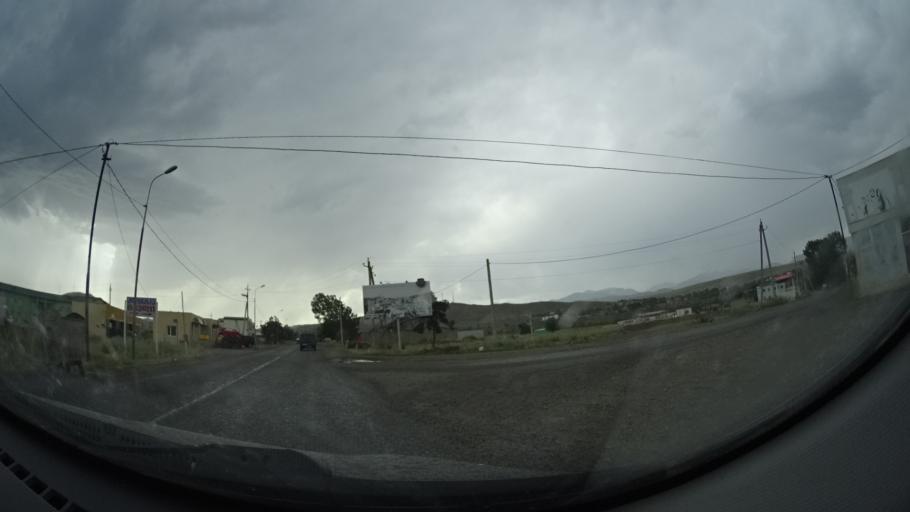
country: GE
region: Samtskhe-Javakheti
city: Akhaltsikhe
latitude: 41.6423
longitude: 43.0120
